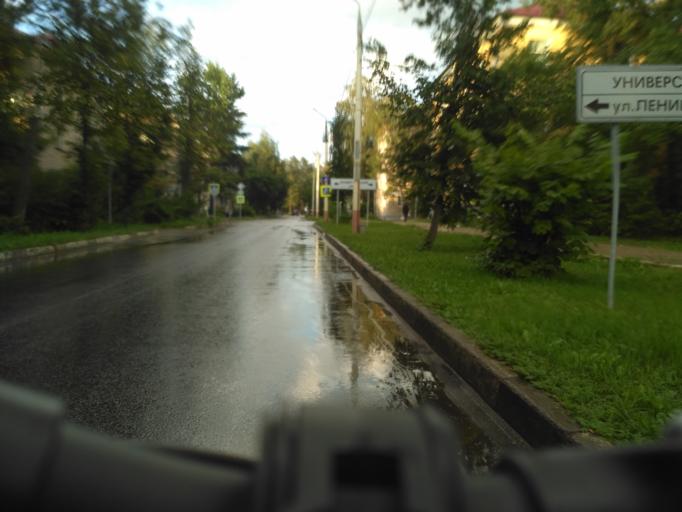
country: RU
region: Moskovskaya
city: Dubna
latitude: 56.7485
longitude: 37.2021
